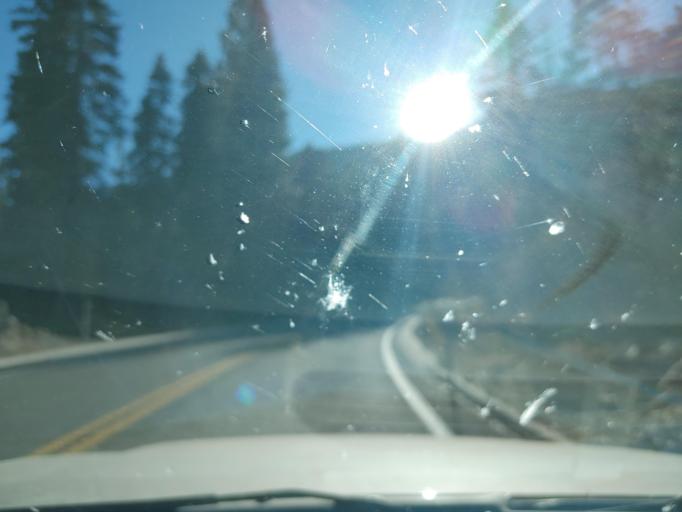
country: US
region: California
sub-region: Placer County
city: Tahoma
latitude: 38.9927
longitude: -120.1087
